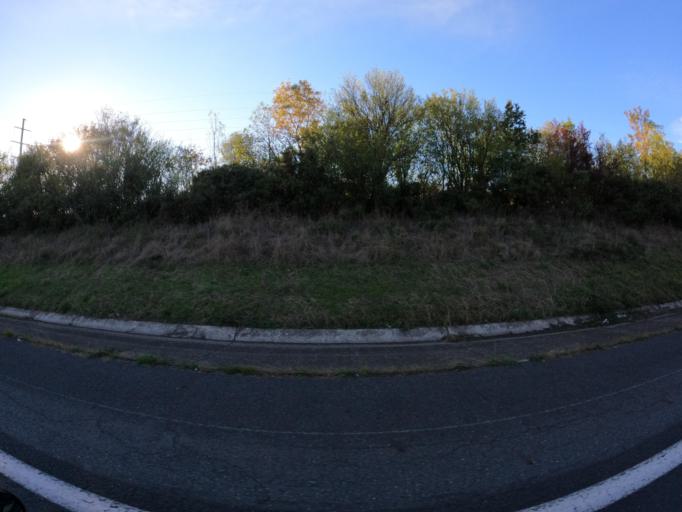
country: FR
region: Pays de la Loire
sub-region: Departement de Maine-et-Loire
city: Mazieres-en-Mauges
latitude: 47.0603
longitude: -0.8295
